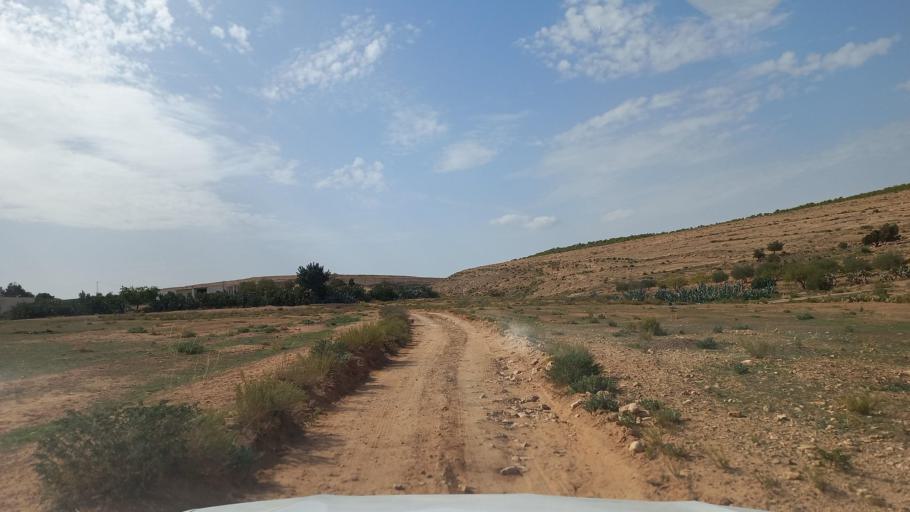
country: TN
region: Al Qasrayn
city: Kasserine
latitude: 35.3651
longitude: 8.8556
